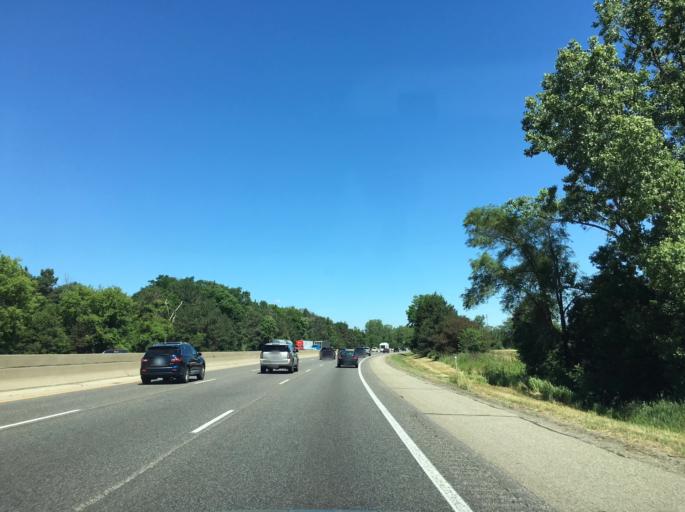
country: US
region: Michigan
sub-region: Genesee County
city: Flint
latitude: 43.0233
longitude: -83.7526
